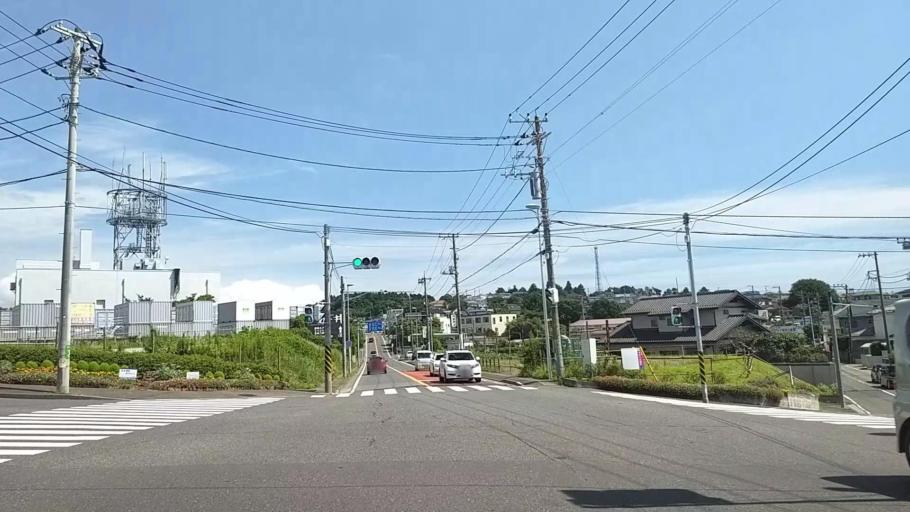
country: JP
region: Kanagawa
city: Fujisawa
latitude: 35.3751
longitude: 139.5071
